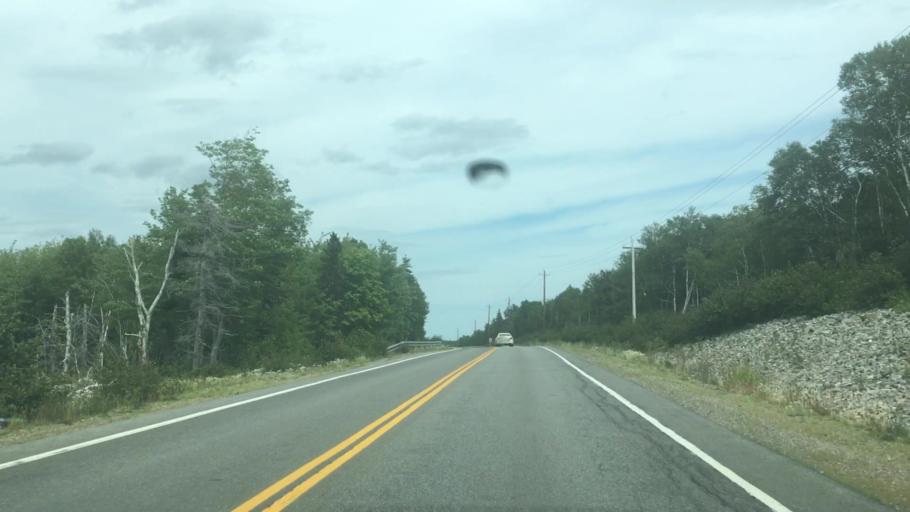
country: CA
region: Nova Scotia
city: Sydney Mines
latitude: 46.5026
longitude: -60.4371
